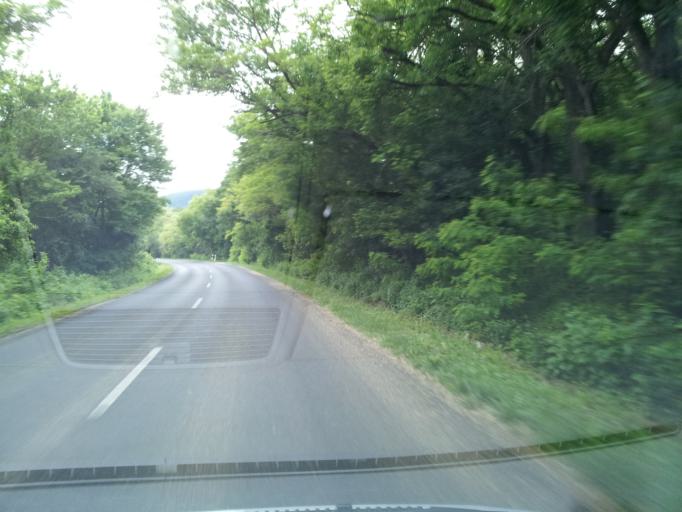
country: HU
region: Pest
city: Csobanka
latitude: 47.6771
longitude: 18.9445
